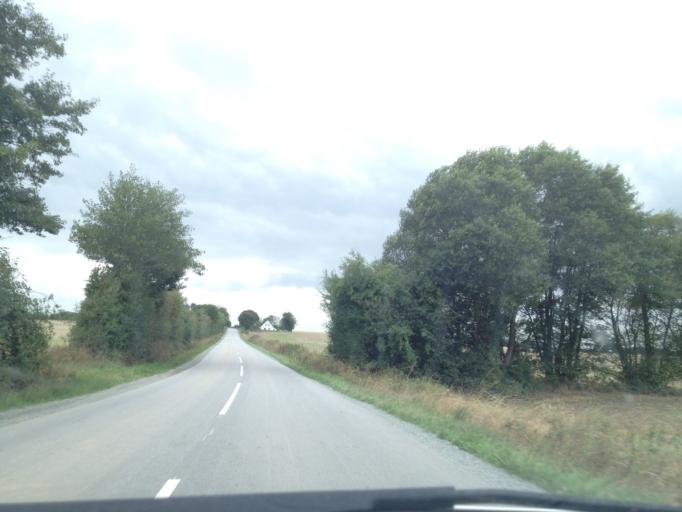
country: DK
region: South Denmark
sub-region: Haderslev Kommune
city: Starup
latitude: 55.3069
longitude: 9.5295
